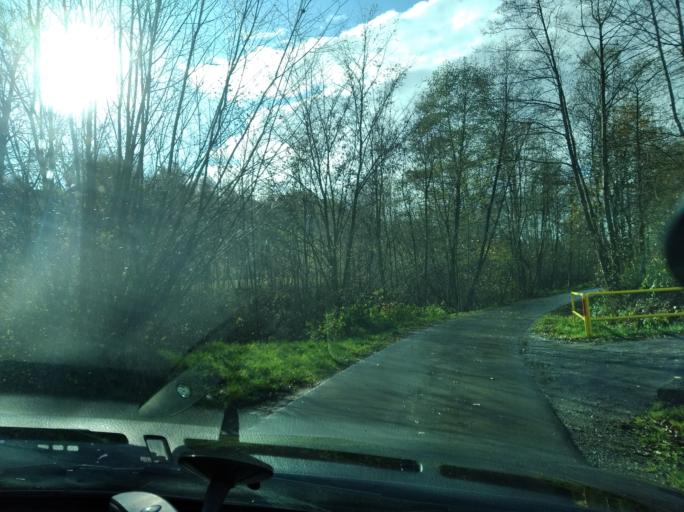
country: PL
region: Subcarpathian Voivodeship
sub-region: Powiat ropczycko-sedziszowski
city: Niedzwiada
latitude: 50.0243
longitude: 21.4781
